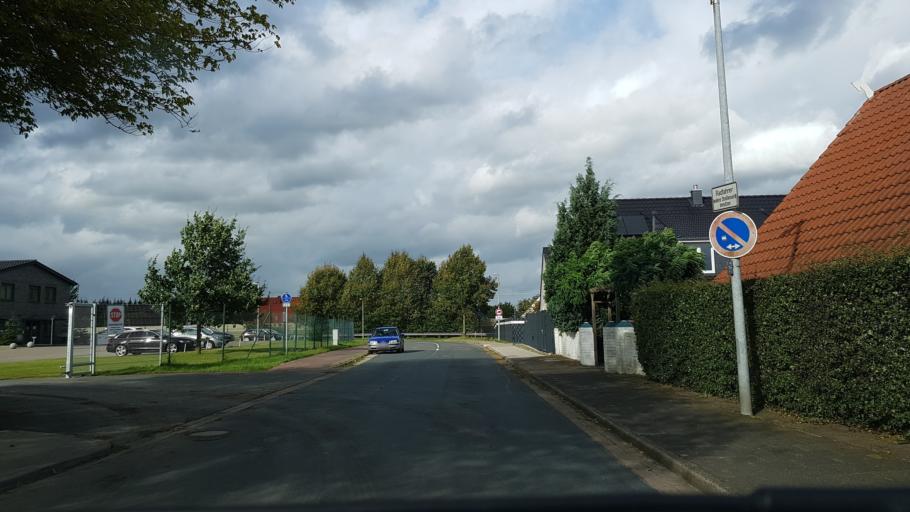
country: DE
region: Lower Saxony
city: Oyten
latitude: 53.0303
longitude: 8.9719
